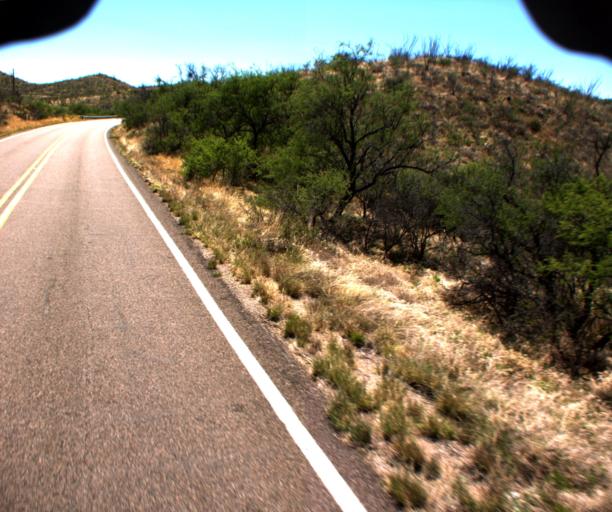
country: US
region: Arizona
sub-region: Pima County
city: Corona de Tucson
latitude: 31.8734
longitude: -110.6770
